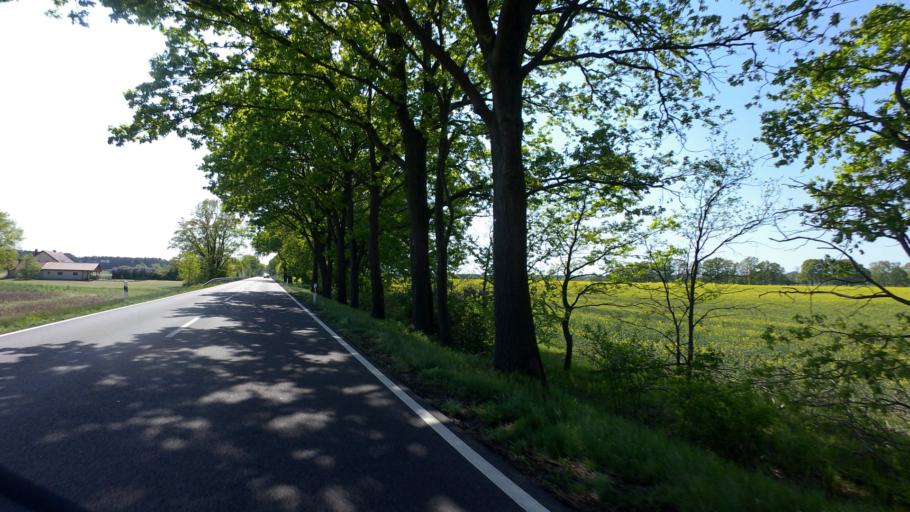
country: DE
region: Brandenburg
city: Neu Zauche
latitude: 52.0204
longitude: 14.0760
